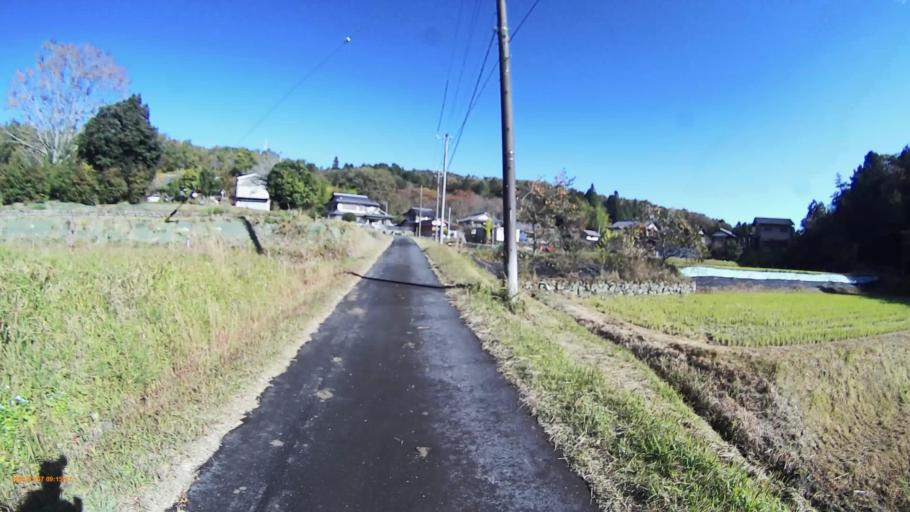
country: JP
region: Gifu
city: Mizunami
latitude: 35.4457
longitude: 137.3555
